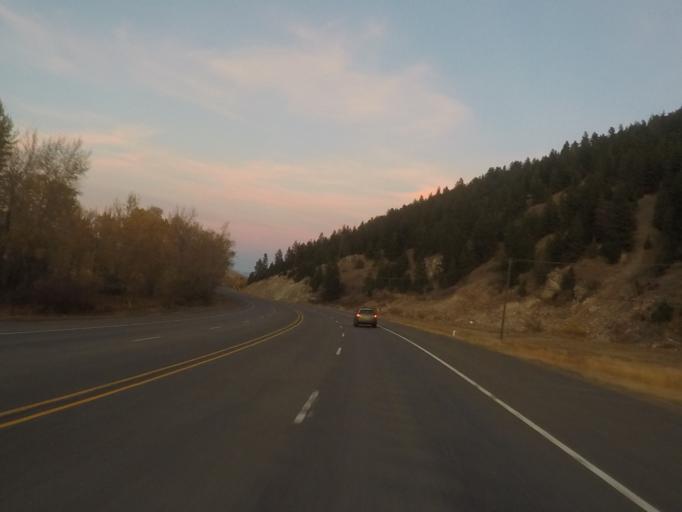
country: US
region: Montana
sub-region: Lewis and Clark County
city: Helena West Side
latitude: 46.5901
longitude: -112.1182
